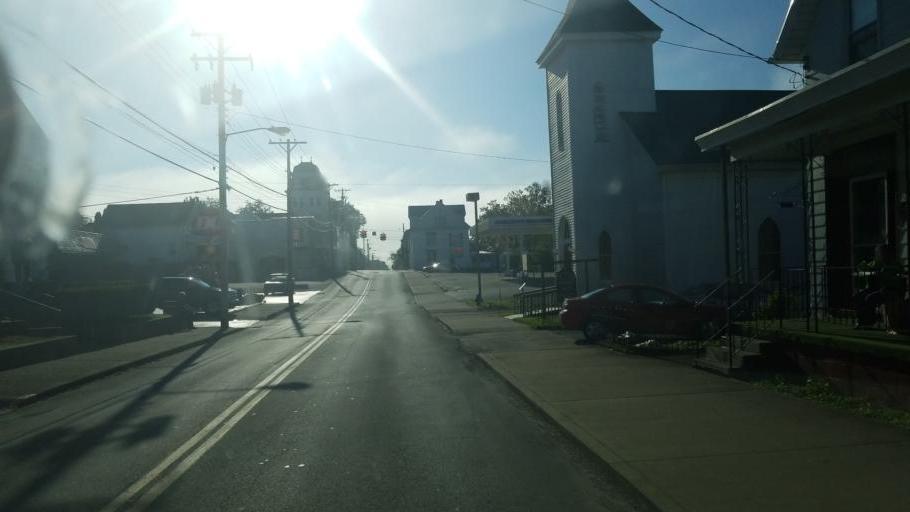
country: US
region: Kentucky
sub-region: Fleming County
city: Flemingsburg
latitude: 38.4215
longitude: -83.7329
